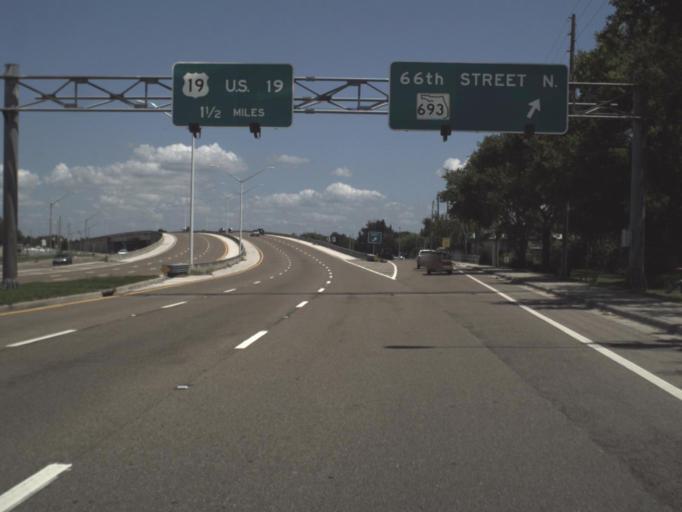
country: US
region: Florida
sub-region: Pinellas County
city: Pinellas Park
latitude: 27.8720
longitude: -82.7333
